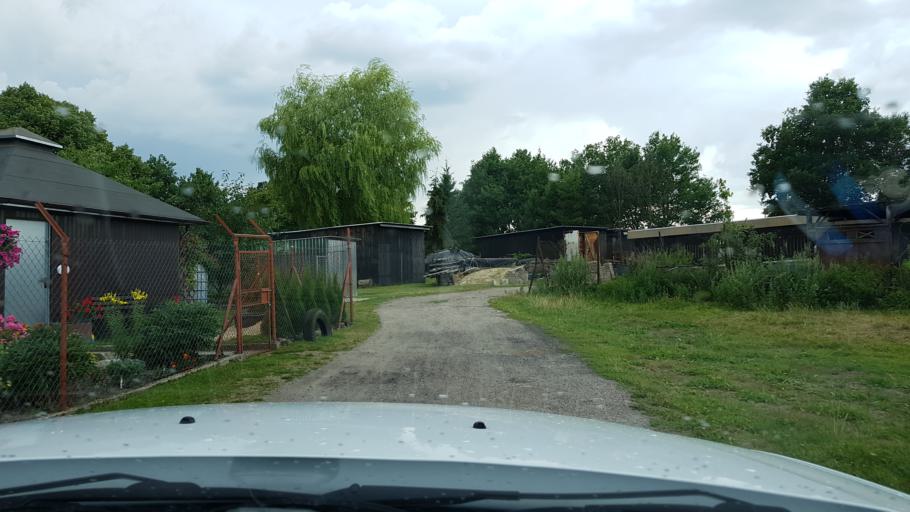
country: PL
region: West Pomeranian Voivodeship
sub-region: Powiat walecki
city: Walcz
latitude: 53.3493
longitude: 16.3921
